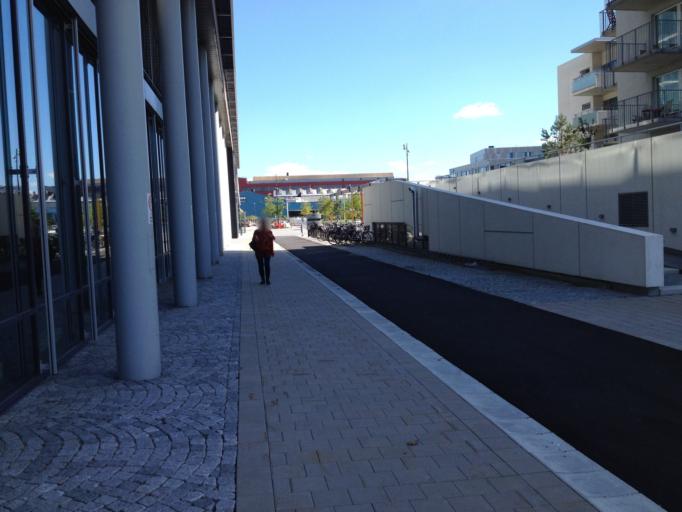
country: SE
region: Skane
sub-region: Malmo
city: Malmoe
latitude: 55.6093
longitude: 12.9784
